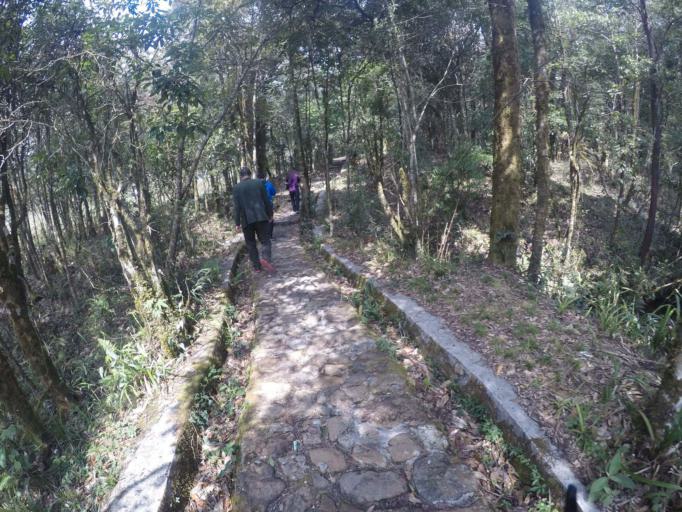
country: VN
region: Lao Cai
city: Sa Pa
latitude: 22.3501
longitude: 103.7719
